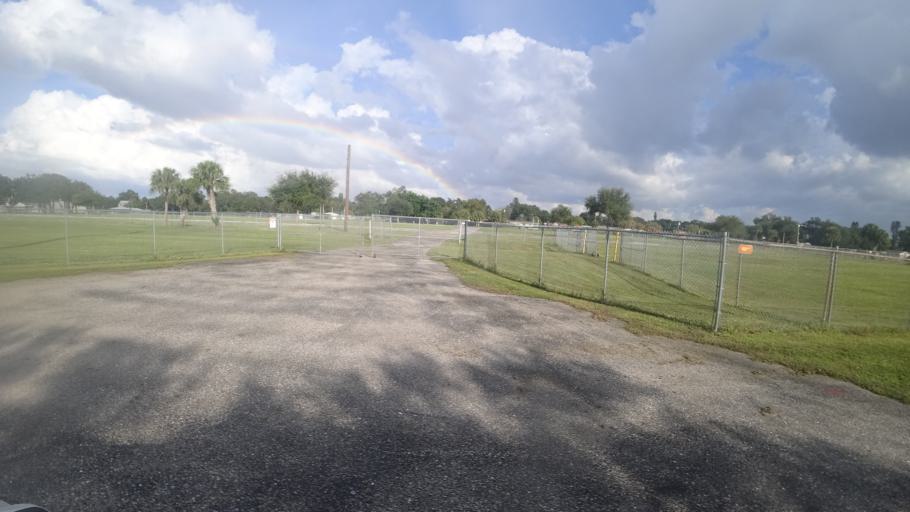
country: US
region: Florida
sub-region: Manatee County
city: Palmetto
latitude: 27.5239
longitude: -82.5812
